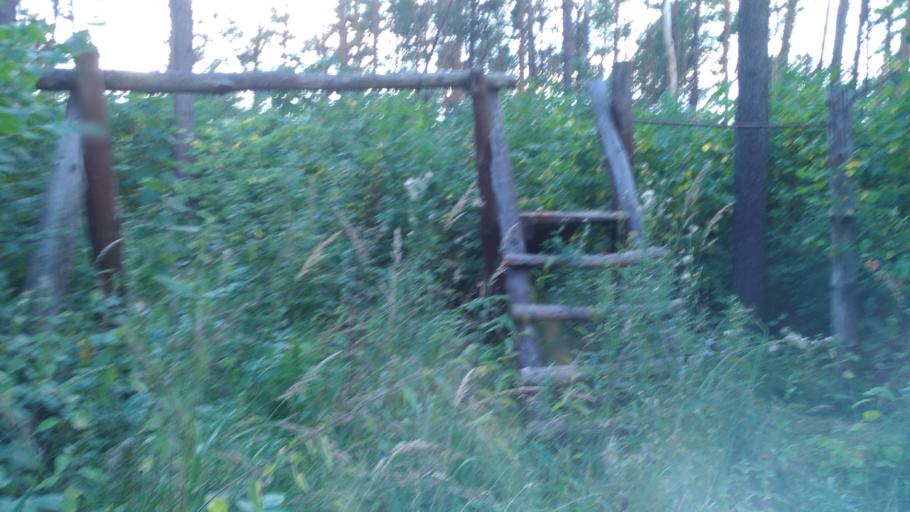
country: LT
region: Vilnius County
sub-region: Trakai
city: Rudiskes
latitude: 54.6257
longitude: 24.8231
